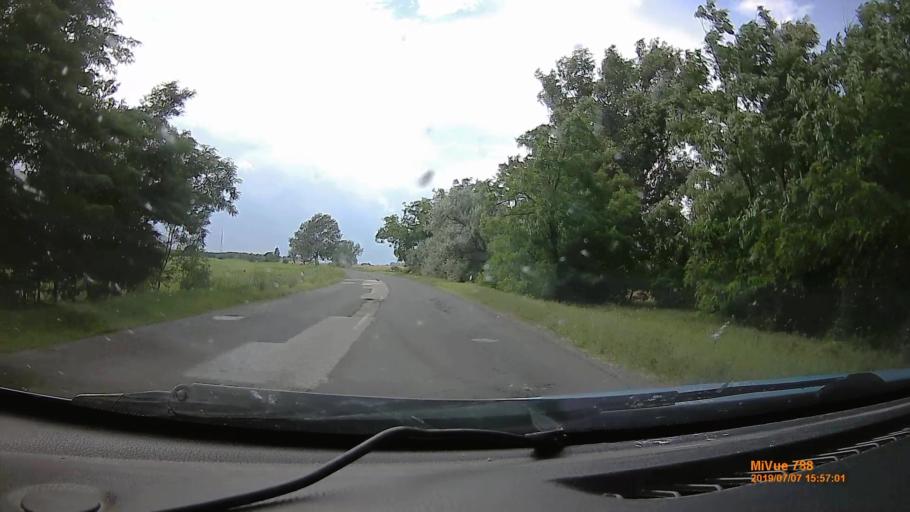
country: HU
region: Pest
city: Szentlorinckata
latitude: 47.5735
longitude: 19.7671
